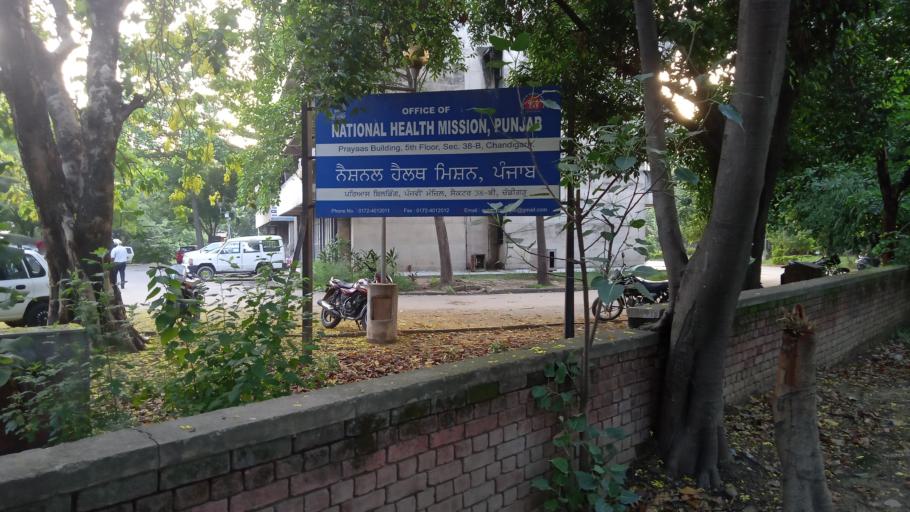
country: IN
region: Chandigarh
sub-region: Chandigarh
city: Chandigarh
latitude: 30.7463
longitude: 76.7525
